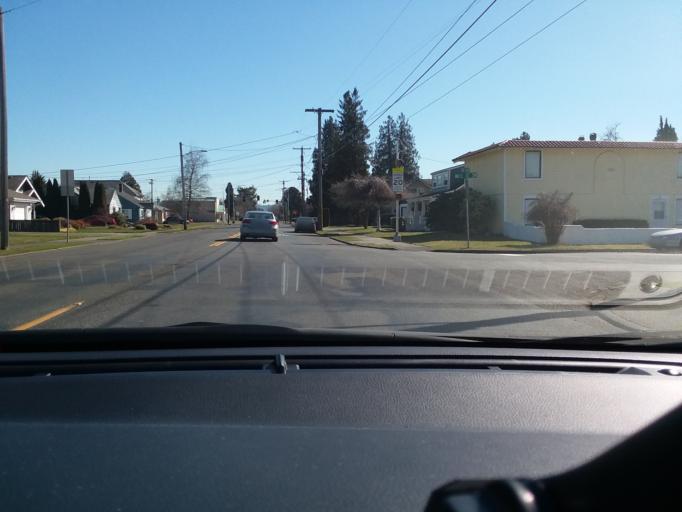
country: US
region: Washington
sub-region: Pierce County
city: Puyallup
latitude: 47.1903
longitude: -122.3117
